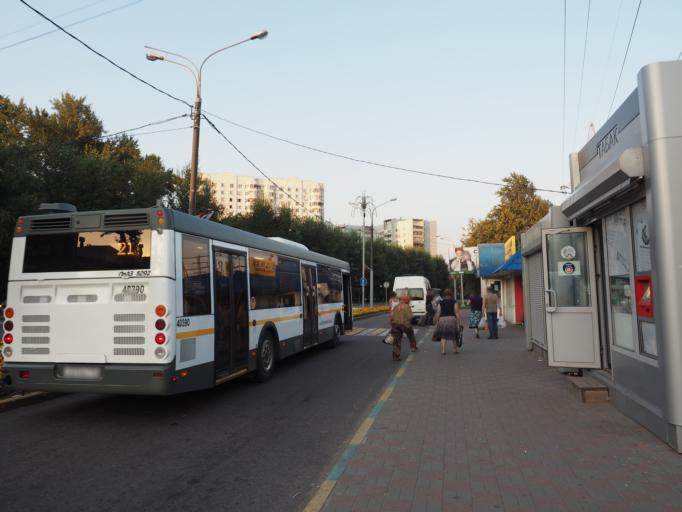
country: RU
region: Moskovskaya
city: Lyubertsy
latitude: 55.6617
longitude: 37.8677
